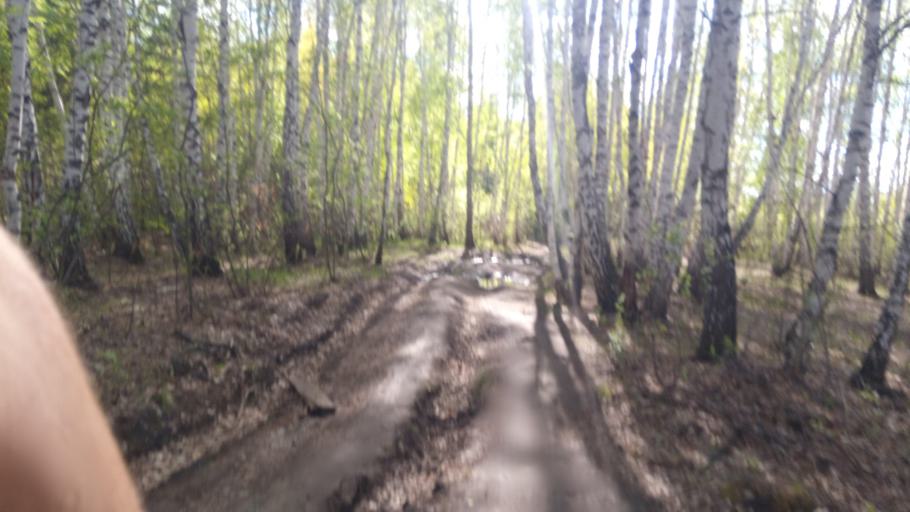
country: RU
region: Chelyabinsk
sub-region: Gorod Chelyabinsk
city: Chelyabinsk
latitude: 55.1683
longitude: 61.3288
